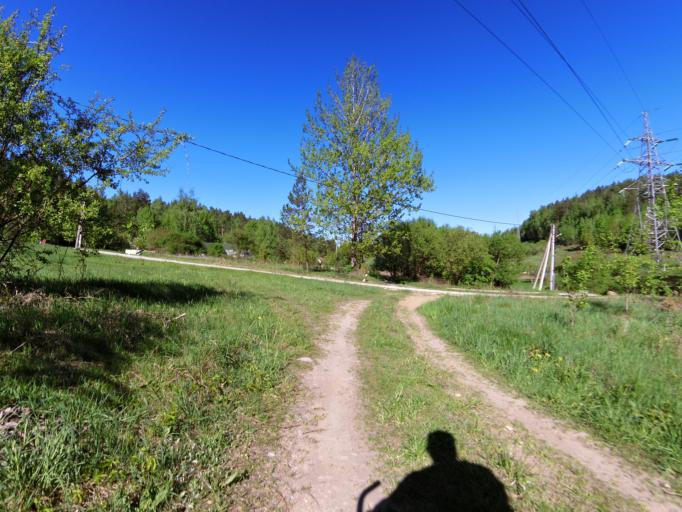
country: LT
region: Vilnius County
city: Pilaite
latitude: 54.6808
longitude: 25.1749
